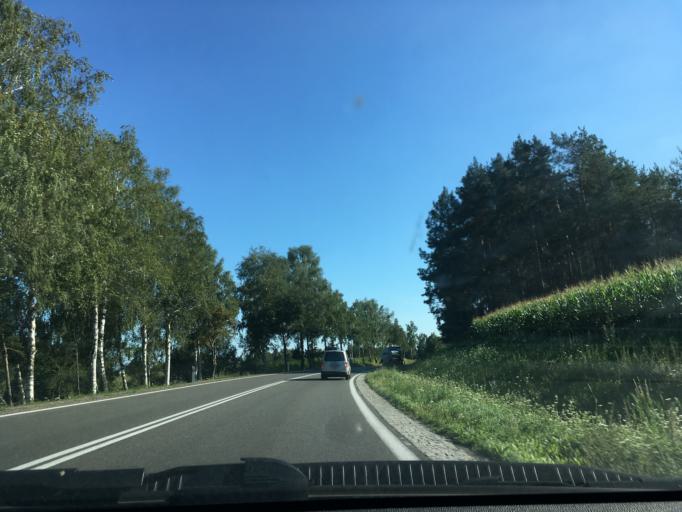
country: PL
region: Podlasie
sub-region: Powiat sokolski
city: Janow
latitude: 53.4120
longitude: 23.1182
